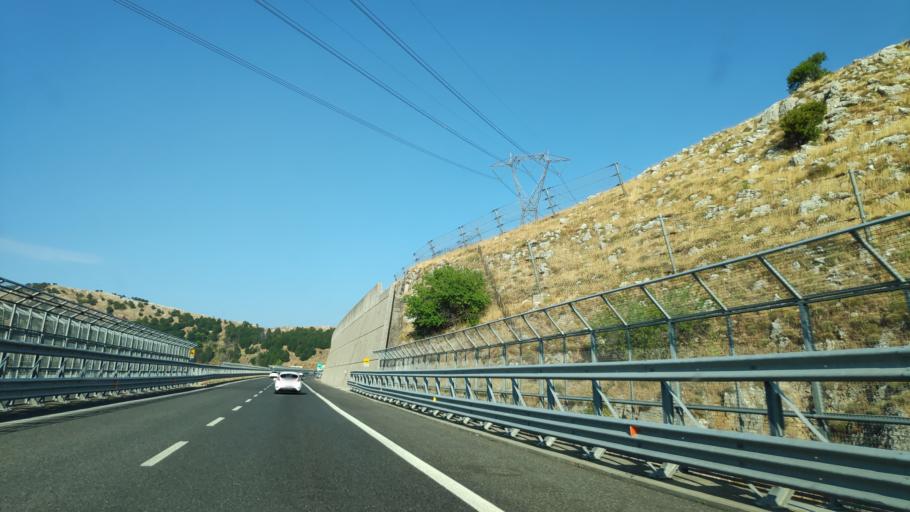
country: IT
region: Calabria
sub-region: Provincia di Cosenza
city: Morano Calabro
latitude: 39.8681
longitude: 16.1090
